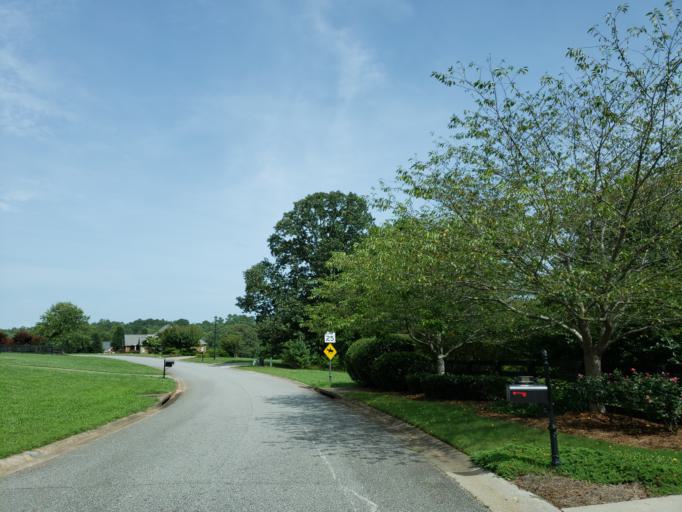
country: US
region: Georgia
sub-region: Cherokee County
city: Ball Ground
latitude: 34.3098
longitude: -84.4447
